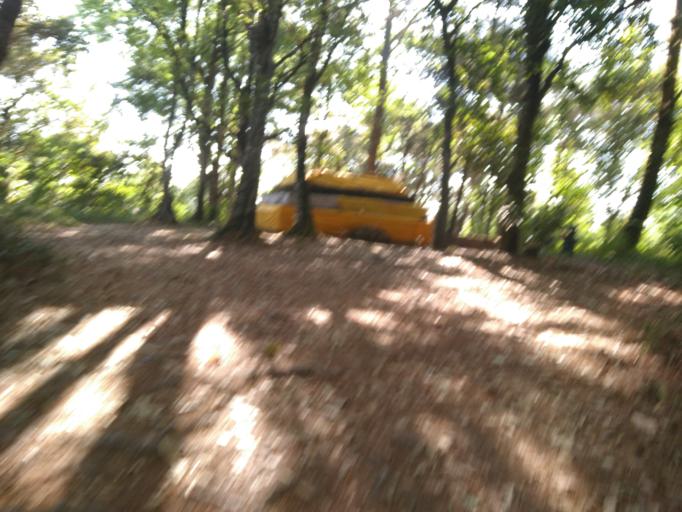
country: TH
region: Chiang Mai
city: Chiang Mai
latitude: 18.8150
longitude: 98.8953
